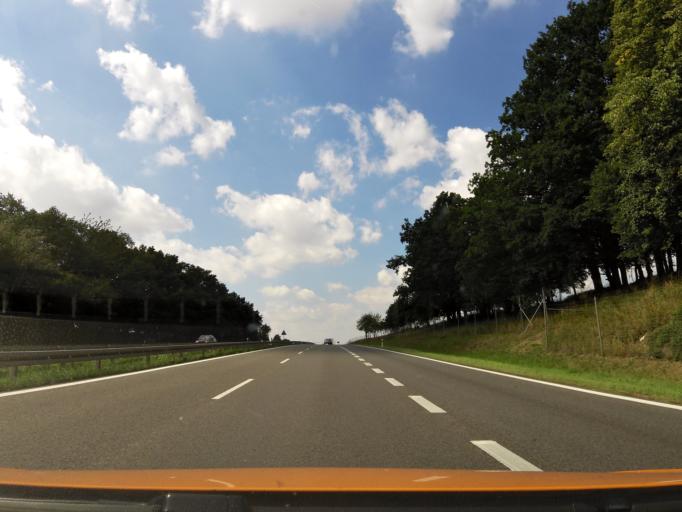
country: PL
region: West Pomeranian Voivodeship
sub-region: Powiat policki
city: Przeclaw
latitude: 53.3417
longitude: 14.4775
